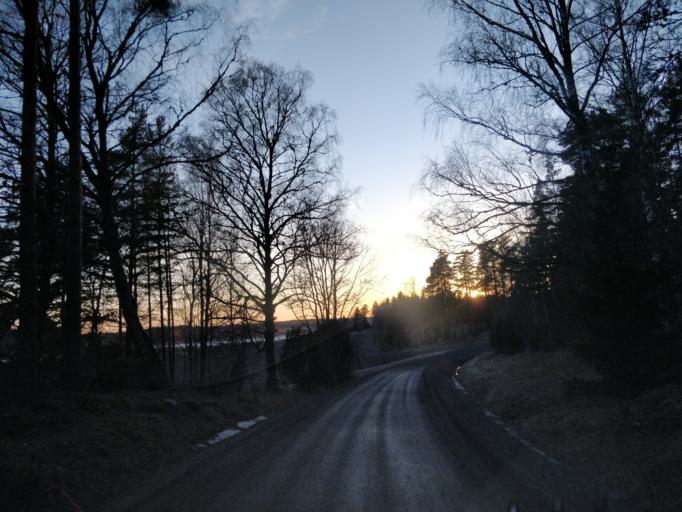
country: SE
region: Uppsala
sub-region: Enkopings Kommun
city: Orsundsbro
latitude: 59.8246
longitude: 17.1539
